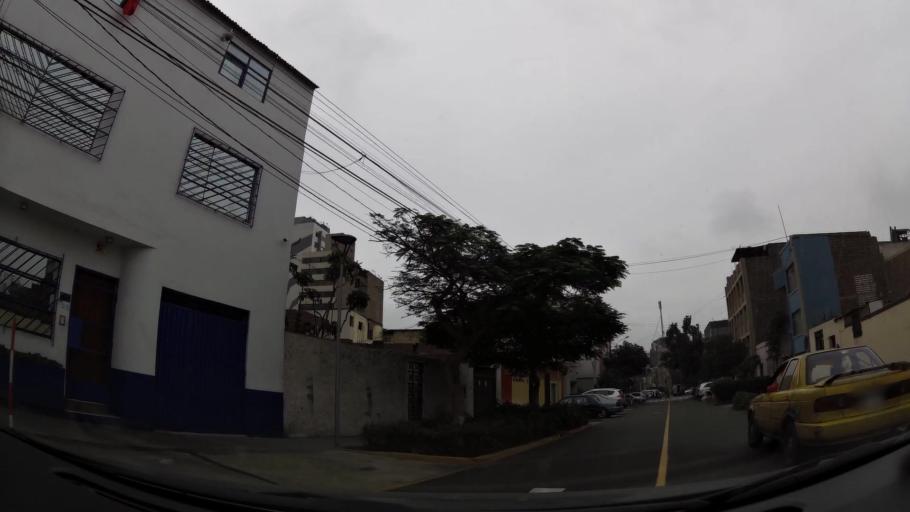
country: PE
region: Lima
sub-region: Lima
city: San Isidro
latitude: -12.0909
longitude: -77.0317
